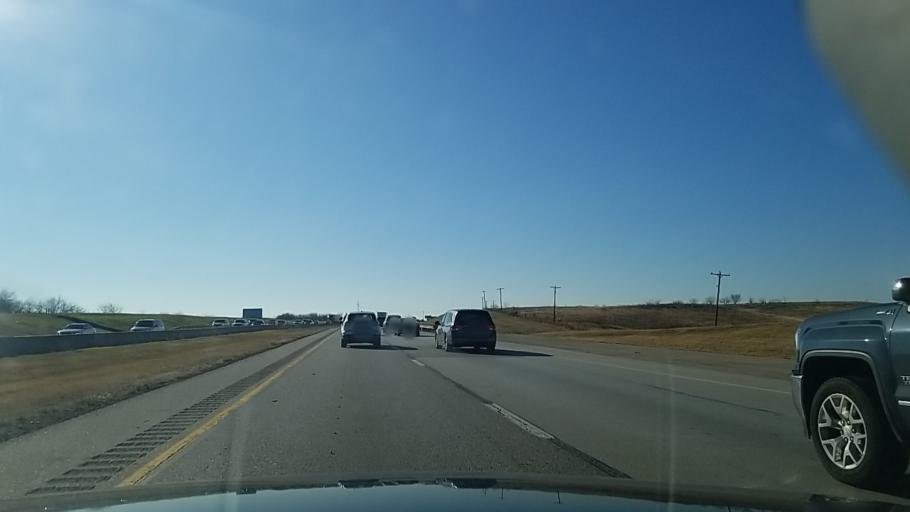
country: US
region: Texas
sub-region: Tarrant County
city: Haslet
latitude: 32.9516
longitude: -97.3106
